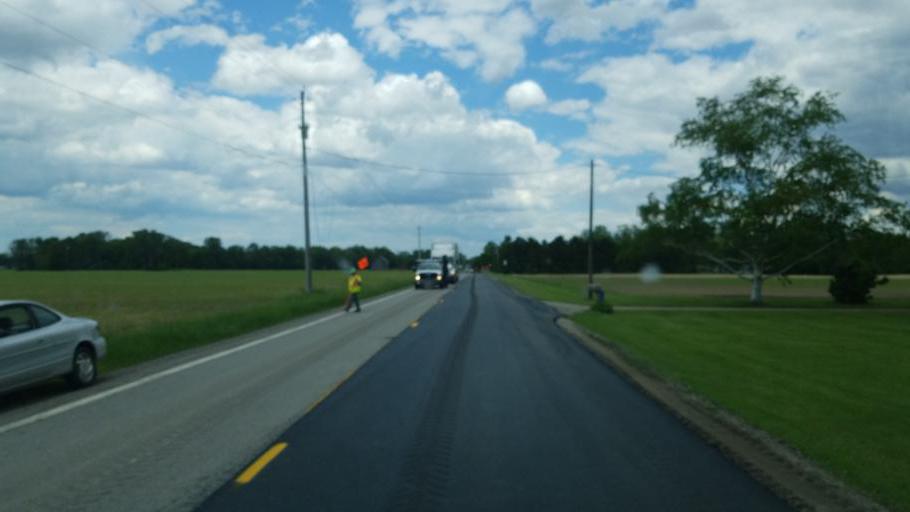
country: US
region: Ohio
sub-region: Erie County
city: Milan
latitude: 41.3001
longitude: -82.6237
